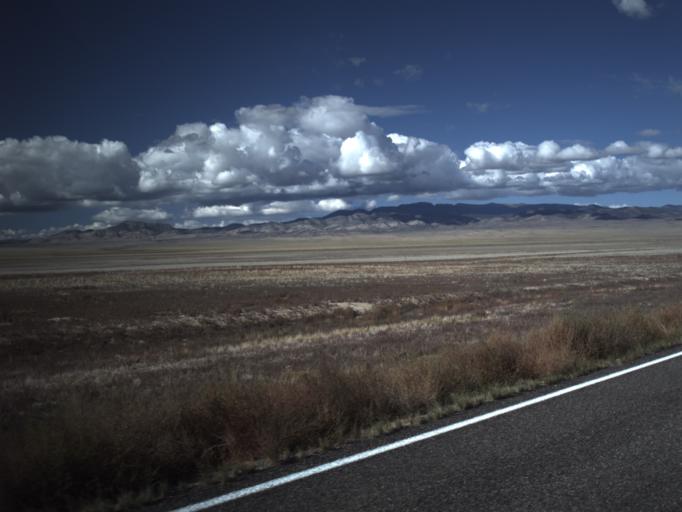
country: US
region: Utah
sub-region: Beaver County
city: Milford
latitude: 38.5192
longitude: -113.6463
